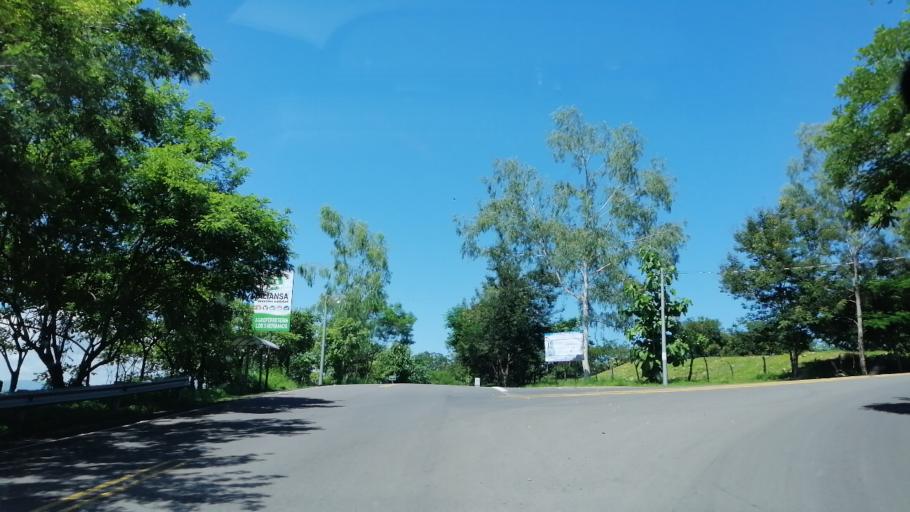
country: SV
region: Morazan
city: Cacaopera
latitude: 13.8089
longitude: -88.1578
